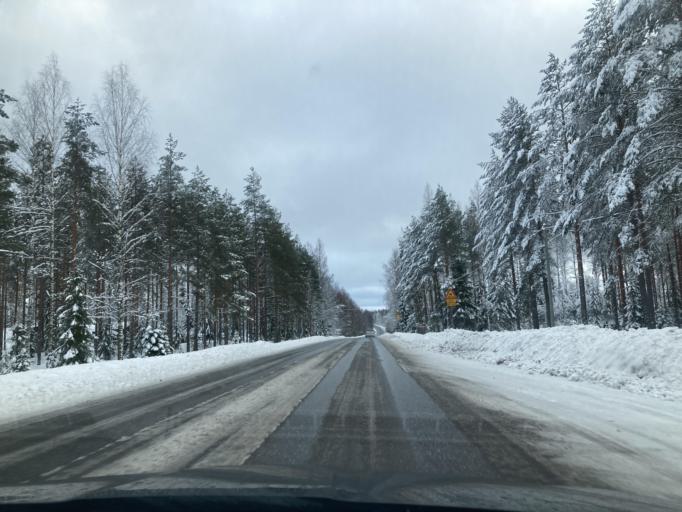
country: FI
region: Paijanne Tavastia
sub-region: Lahti
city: Padasjoki
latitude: 61.3035
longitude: 25.2973
